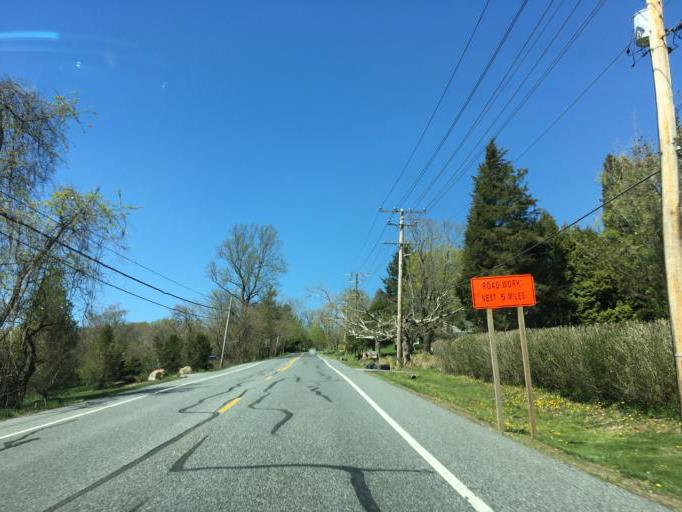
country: US
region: Maryland
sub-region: Baltimore County
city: Hunt Valley
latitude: 39.5450
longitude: -76.6510
